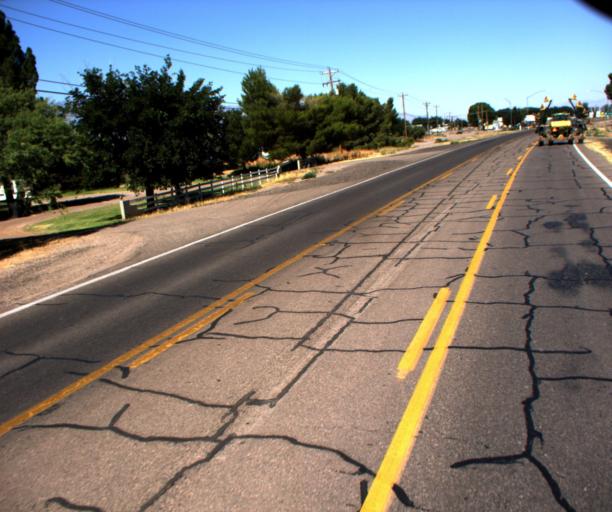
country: US
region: Arizona
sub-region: Graham County
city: Safford
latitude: 32.8167
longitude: -109.6766
